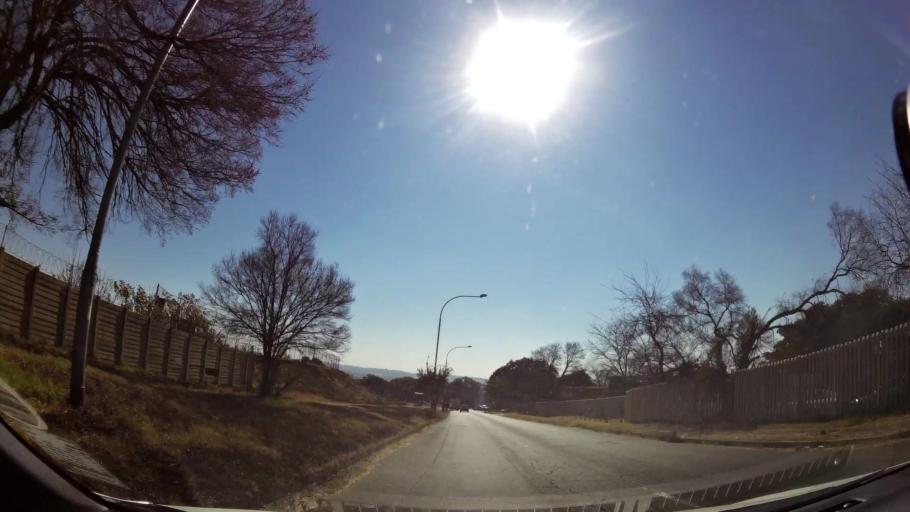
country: ZA
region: Gauteng
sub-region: City of Johannesburg Metropolitan Municipality
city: Johannesburg
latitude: -26.2444
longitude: 28.0887
